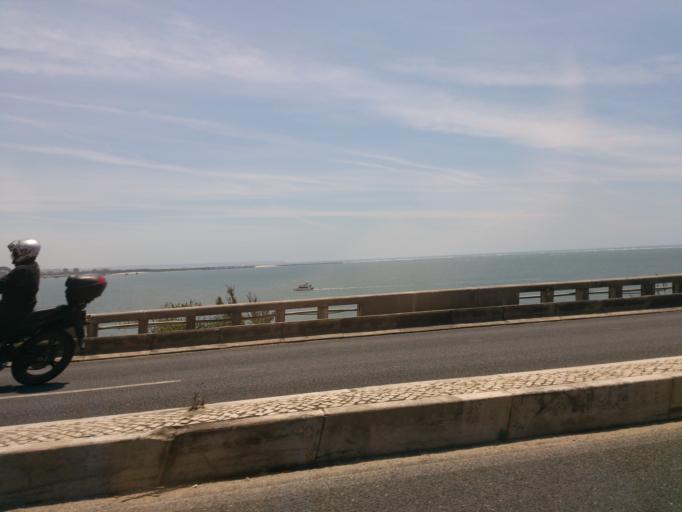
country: PT
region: Lisbon
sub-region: Oeiras
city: Quejas
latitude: 38.6998
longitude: -9.2649
